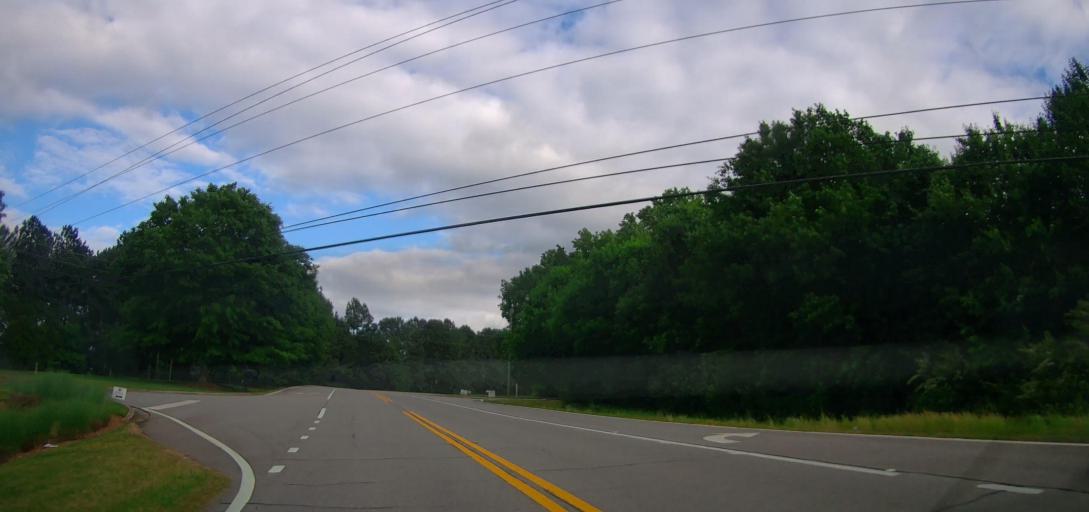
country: US
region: Georgia
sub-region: Oconee County
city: Bogart
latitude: 33.9215
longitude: -83.4639
